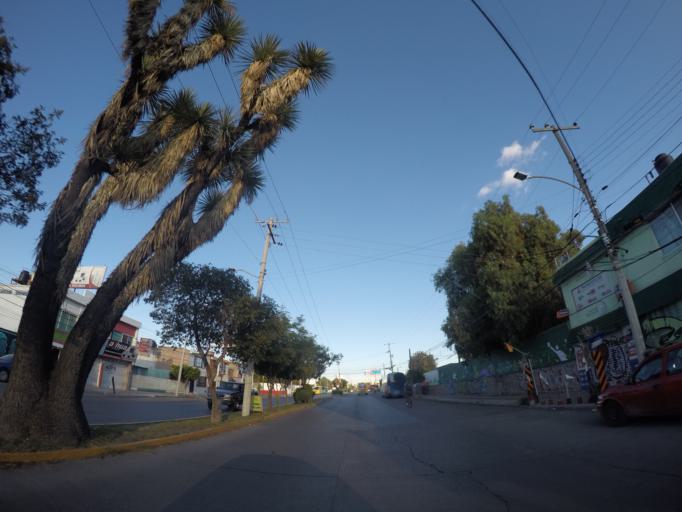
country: MX
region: San Luis Potosi
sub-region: San Luis Potosi
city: San Luis Potosi
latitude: 22.1377
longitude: -100.9864
